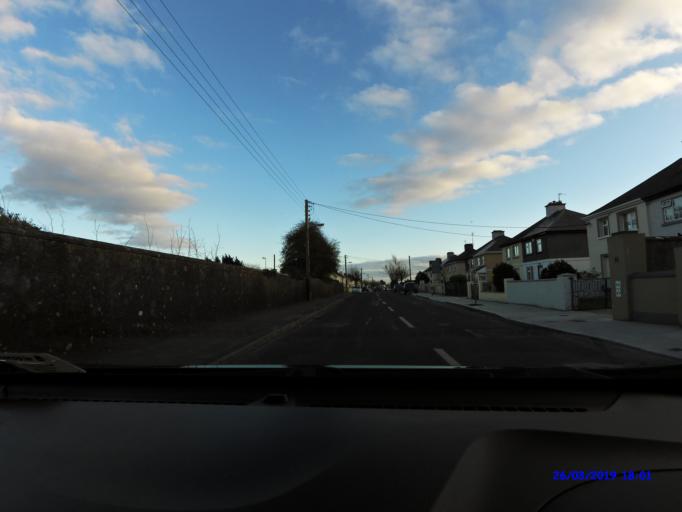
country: IE
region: Connaught
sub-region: County Galway
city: Tuam
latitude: 53.5106
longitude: -8.8450
